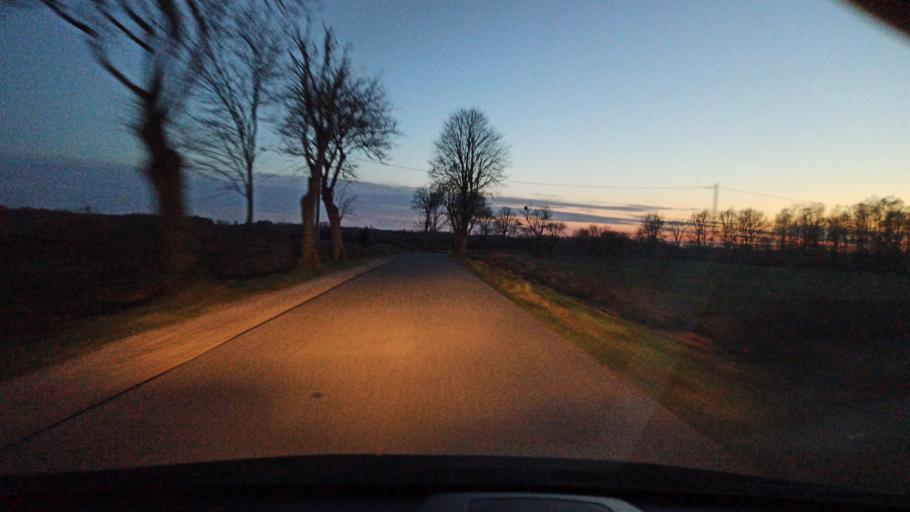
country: PL
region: Warmian-Masurian Voivodeship
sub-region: Powiat elblaski
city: Gronowo Gorne
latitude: 54.1794
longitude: 19.5258
